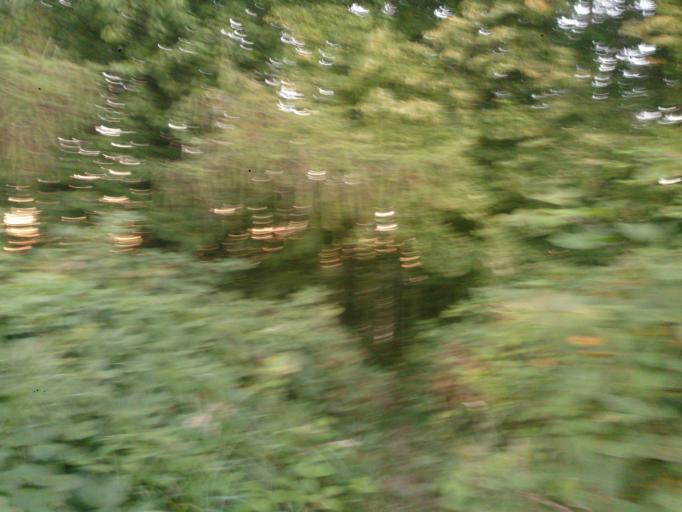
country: PL
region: Pomeranian Voivodeship
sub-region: Gdynia
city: Gdynia
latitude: 54.4780
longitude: 18.5296
